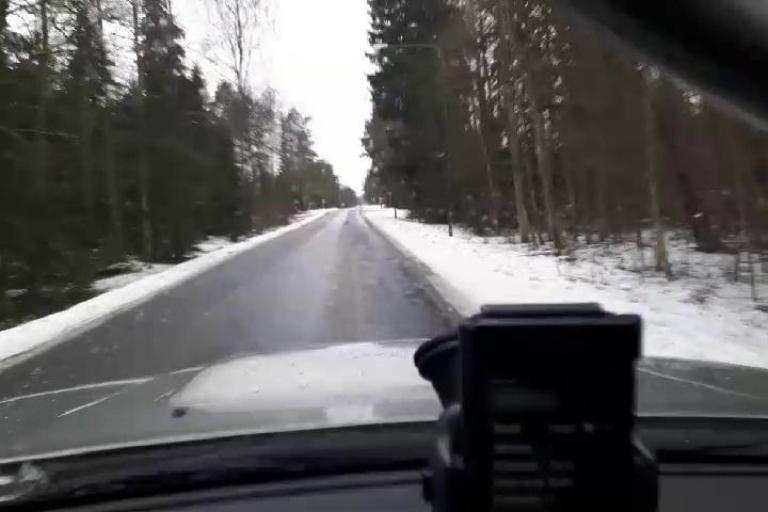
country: EE
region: Harju
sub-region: Harku vald
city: Tabasalu
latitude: 59.4302
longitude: 24.4710
